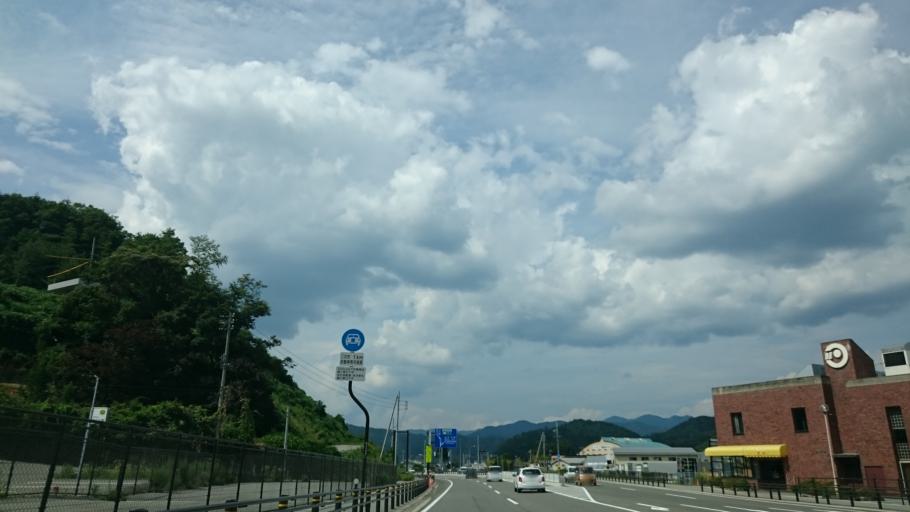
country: JP
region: Gifu
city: Takayama
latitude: 36.1583
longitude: 137.2437
